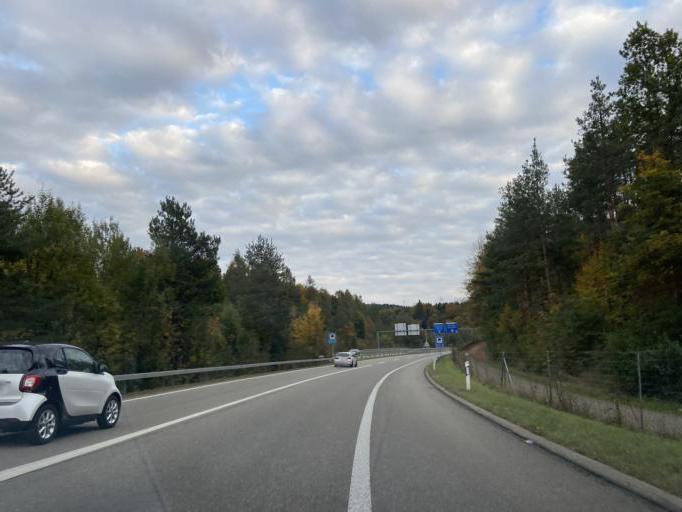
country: CH
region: Zurich
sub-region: Bezirk Pfaeffikon
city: Effretikon / Watt
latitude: 47.4423
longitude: 8.6944
